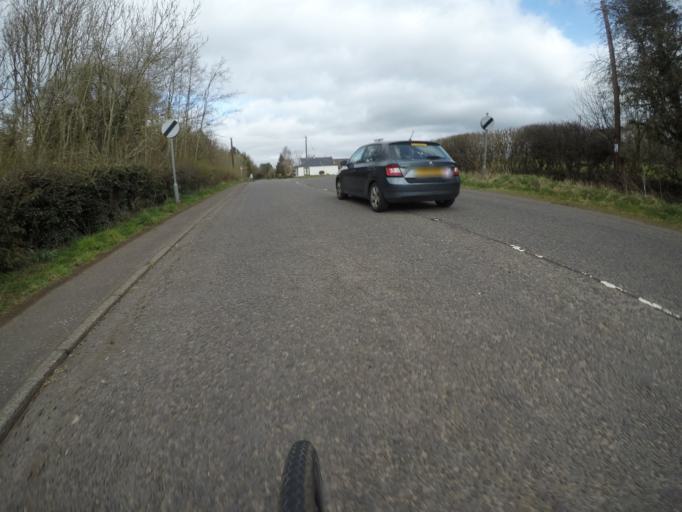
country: GB
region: Scotland
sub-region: North Ayrshire
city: Irvine
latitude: 55.6349
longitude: -4.6332
